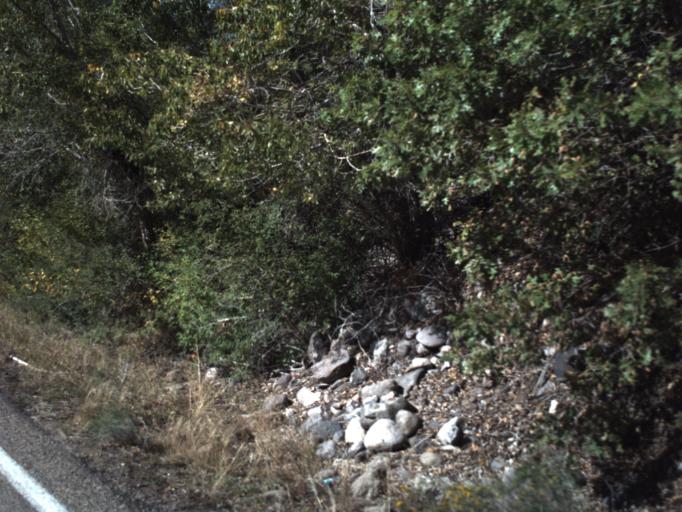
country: US
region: Utah
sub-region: Beaver County
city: Beaver
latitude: 38.2805
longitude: -112.5770
